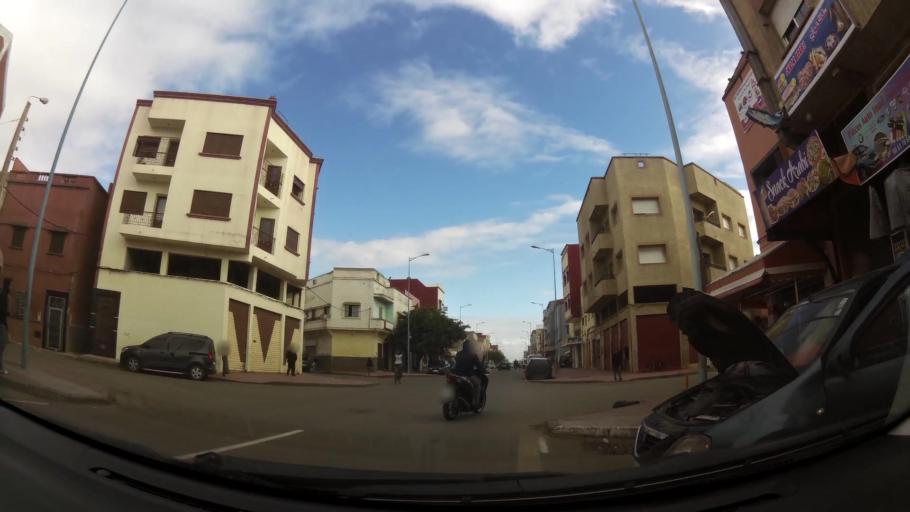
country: MA
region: Doukkala-Abda
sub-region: El-Jadida
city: El Jadida
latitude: 33.2554
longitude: -8.5151
